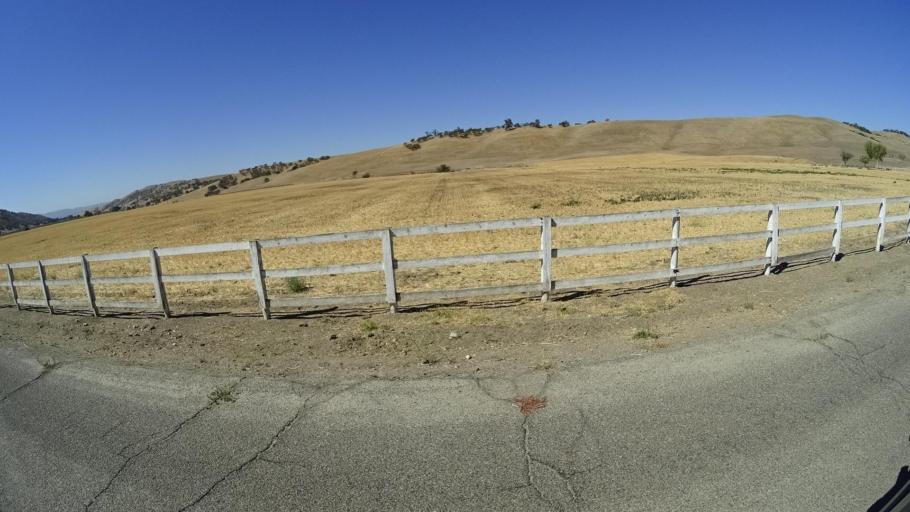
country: US
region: California
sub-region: San Luis Obispo County
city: San Miguel
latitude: 35.8273
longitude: -120.6552
